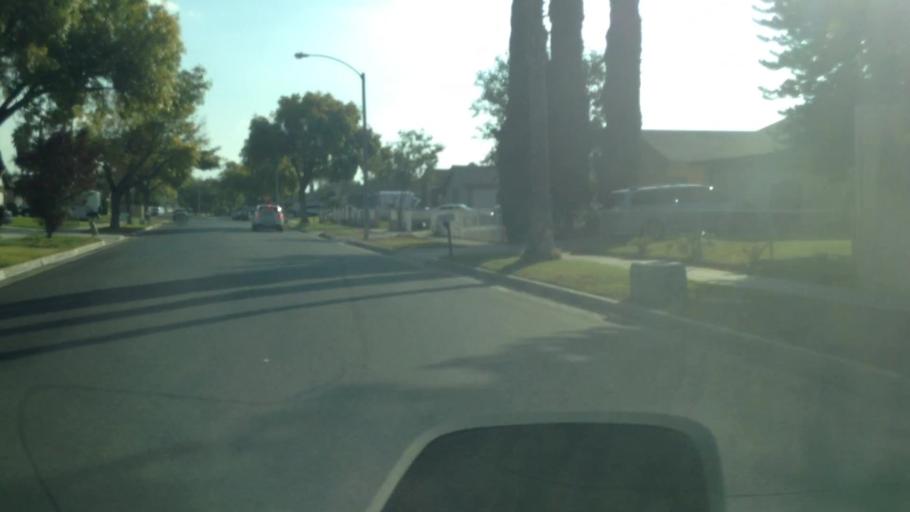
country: US
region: California
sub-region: Riverside County
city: Pedley
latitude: 33.9557
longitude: -117.4692
